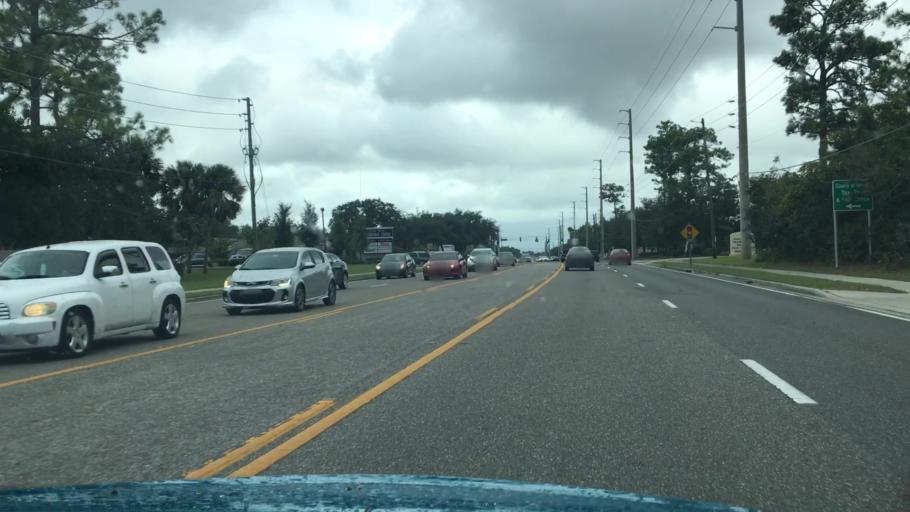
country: US
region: Florida
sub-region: Volusia County
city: Deltona
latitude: 28.9055
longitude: -81.2888
